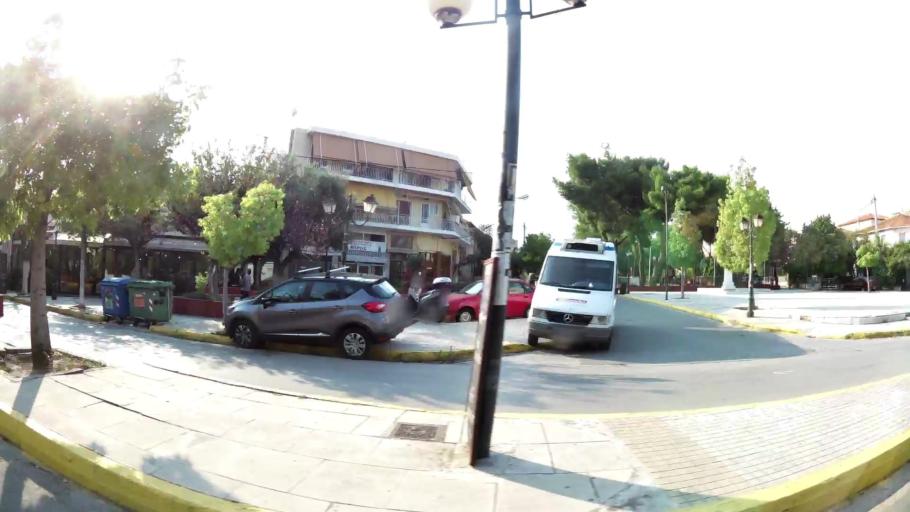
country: GR
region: Attica
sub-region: Nomarchia Athinas
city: Nea Filadelfeia
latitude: 38.0385
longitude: 23.7375
